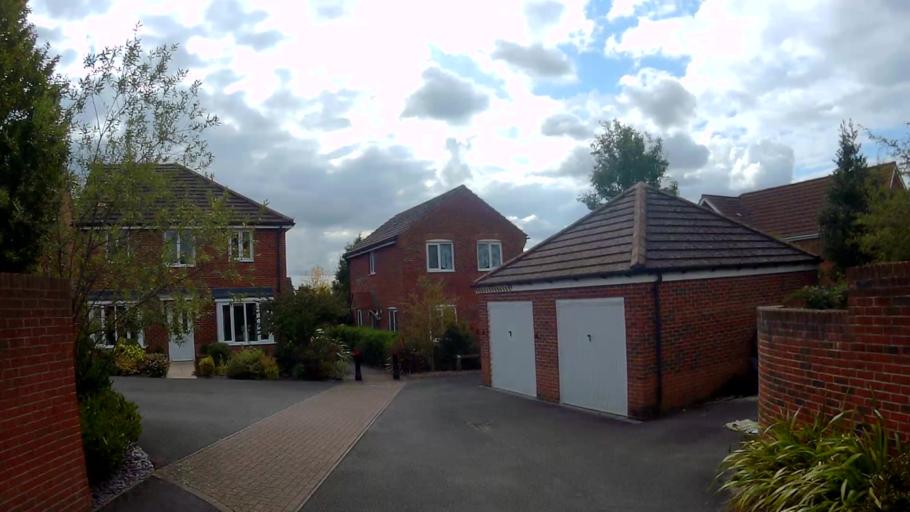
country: GB
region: England
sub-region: Hampshire
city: Overton
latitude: 51.2240
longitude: -1.3309
